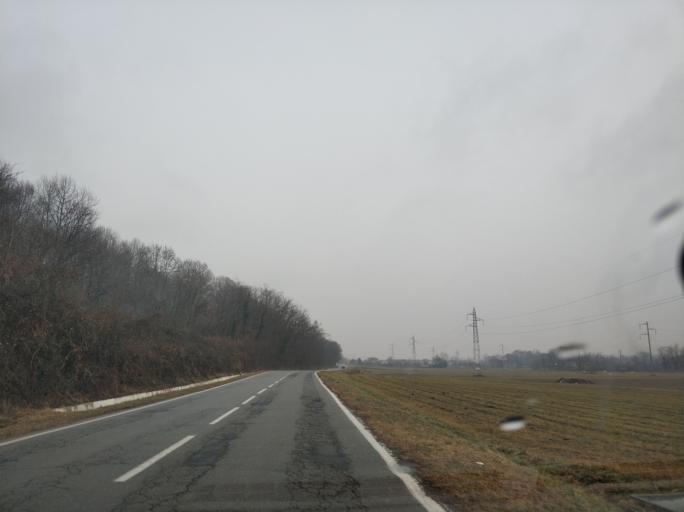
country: IT
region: Piedmont
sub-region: Provincia di Torino
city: San Francesco al Campo
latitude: 45.2268
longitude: 7.6493
